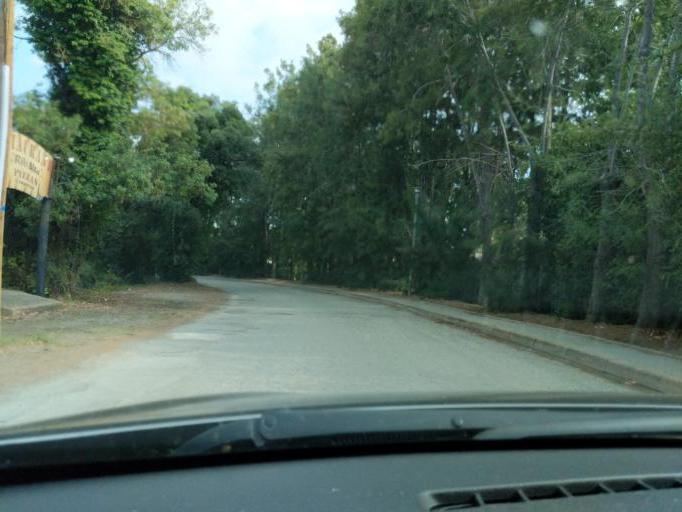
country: FR
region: Corsica
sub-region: Departement de la Haute-Corse
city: Ghisonaccia
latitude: 42.0005
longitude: 9.4440
